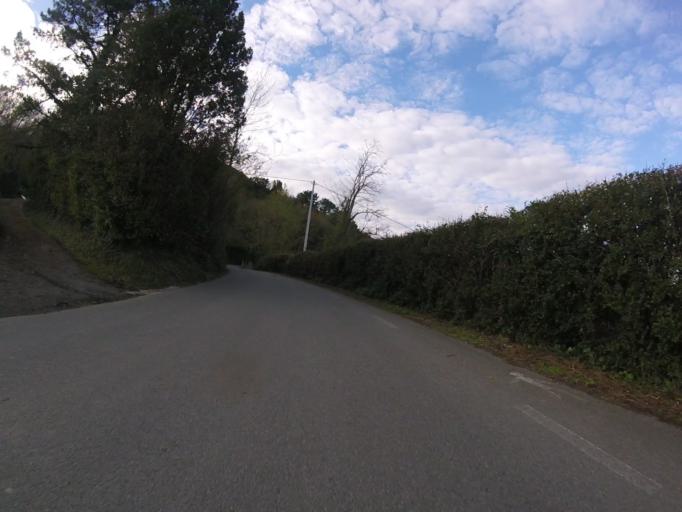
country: ES
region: Basque Country
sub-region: Provincia de Guipuzcoa
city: Errenteria
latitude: 43.3038
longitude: -1.9191
